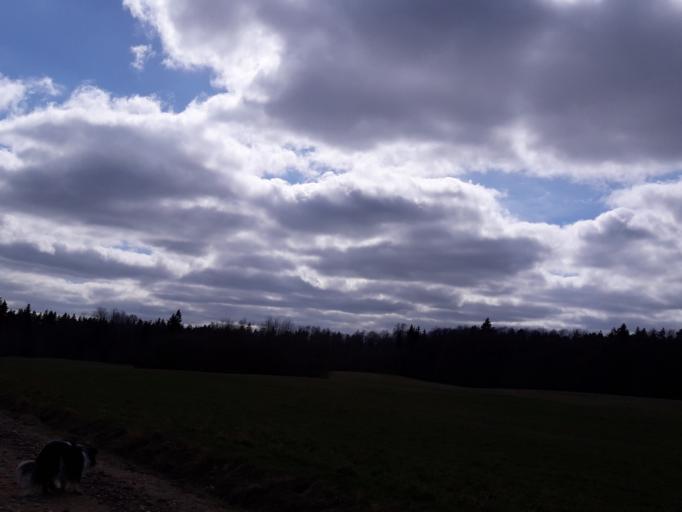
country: LV
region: Talsu Rajons
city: Sabile
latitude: 56.9116
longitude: 22.3985
